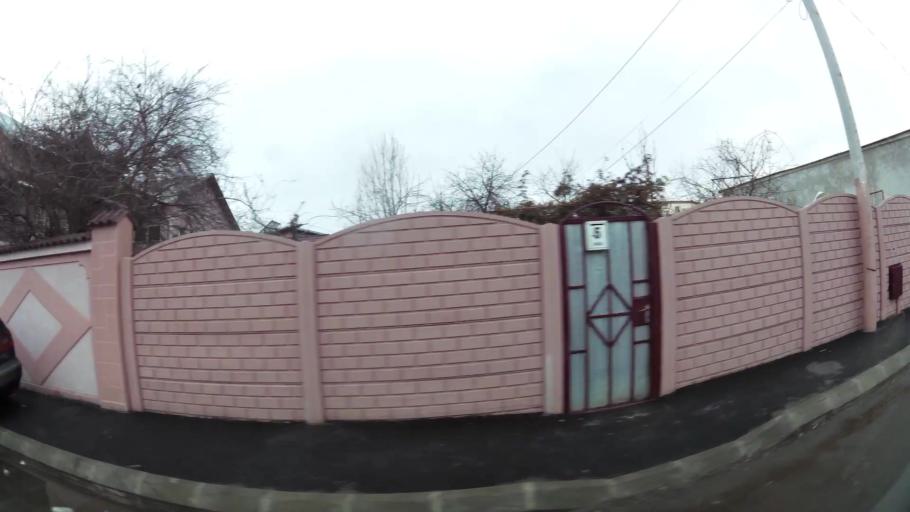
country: RO
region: Ilfov
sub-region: Voluntari City
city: Voluntari
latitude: 44.4814
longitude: 26.1839
